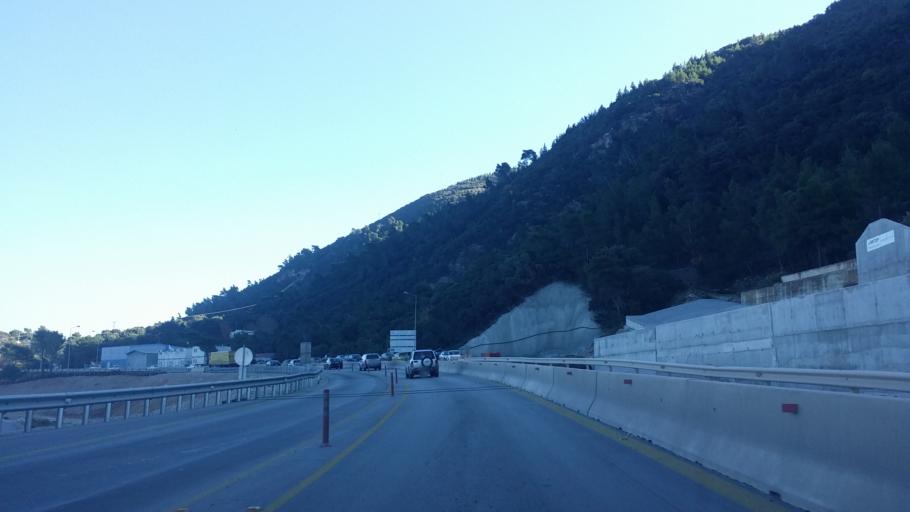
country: GR
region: West Greece
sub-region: Nomos Achaias
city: Kamarai
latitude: 38.3237
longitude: 21.9219
